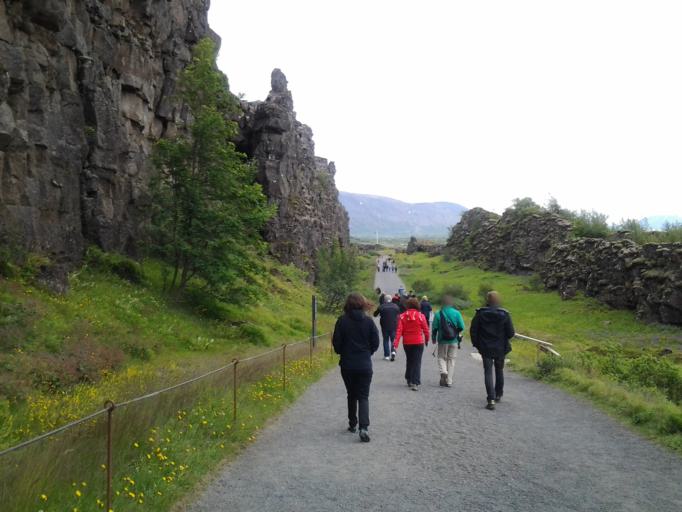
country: IS
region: South
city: Hveragerdi
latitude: 64.2567
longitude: -21.1273
